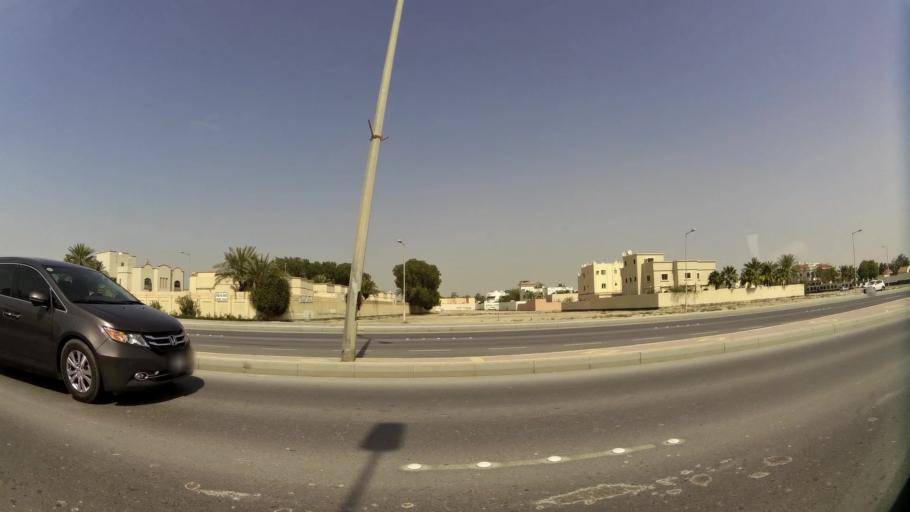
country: BH
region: Northern
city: Madinat `Isa
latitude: 26.1938
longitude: 50.4633
